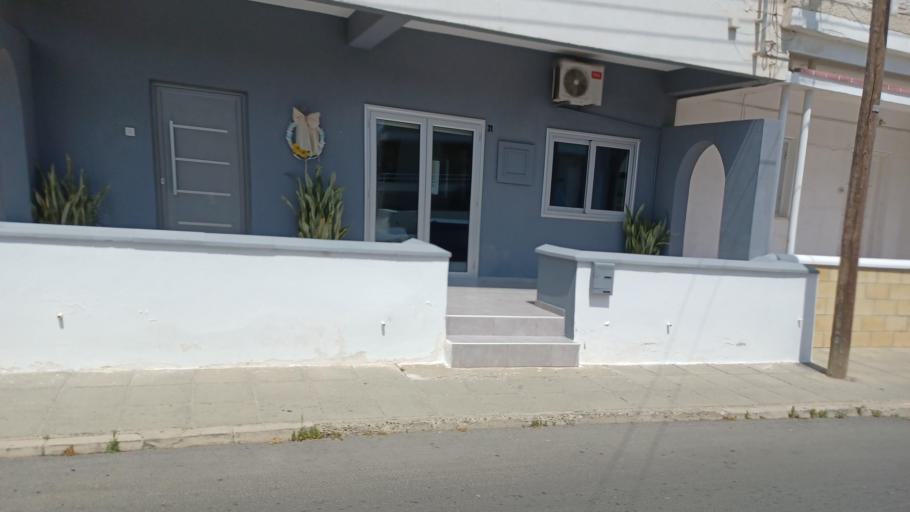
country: CY
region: Ammochostos
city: Paralimni
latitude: 35.0418
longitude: 33.9814
